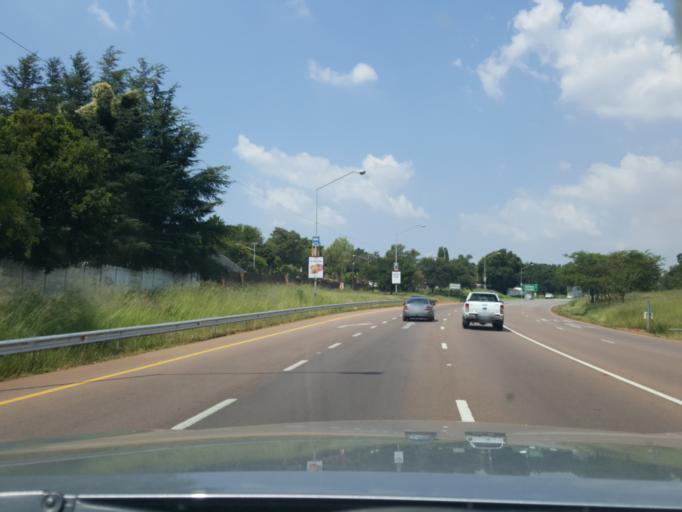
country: ZA
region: Gauteng
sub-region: City of Tshwane Metropolitan Municipality
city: Centurion
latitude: -25.8141
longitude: 28.2362
